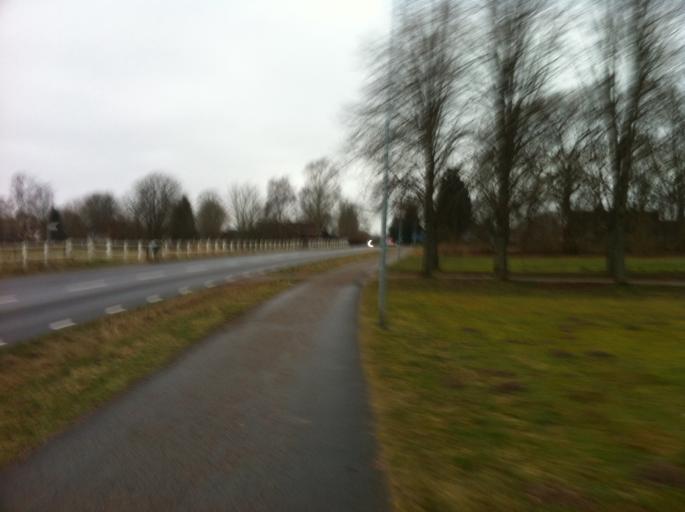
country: SE
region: Skane
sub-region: Hoors Kommun
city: Satofta
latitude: 55.9113
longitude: 13.5519
